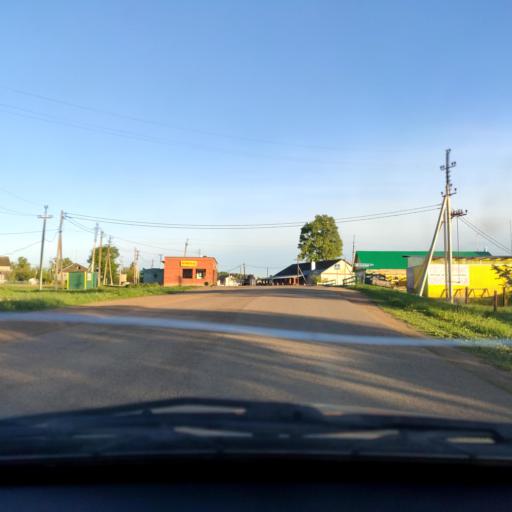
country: RU
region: Bashkortostan
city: Yazykovo
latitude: 55.0475
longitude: 56.1794
